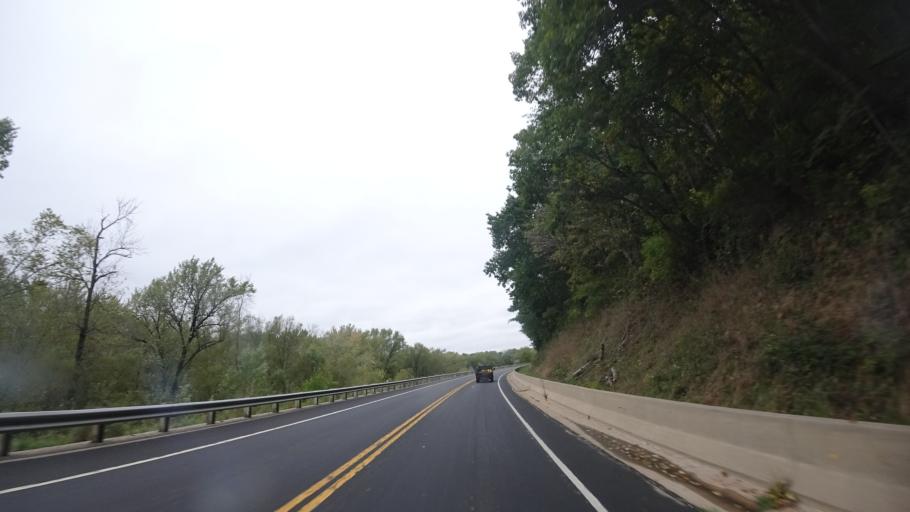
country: US
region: Wisconsin
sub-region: Grant County
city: Boscobel
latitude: 43.1407
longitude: -90.7355
